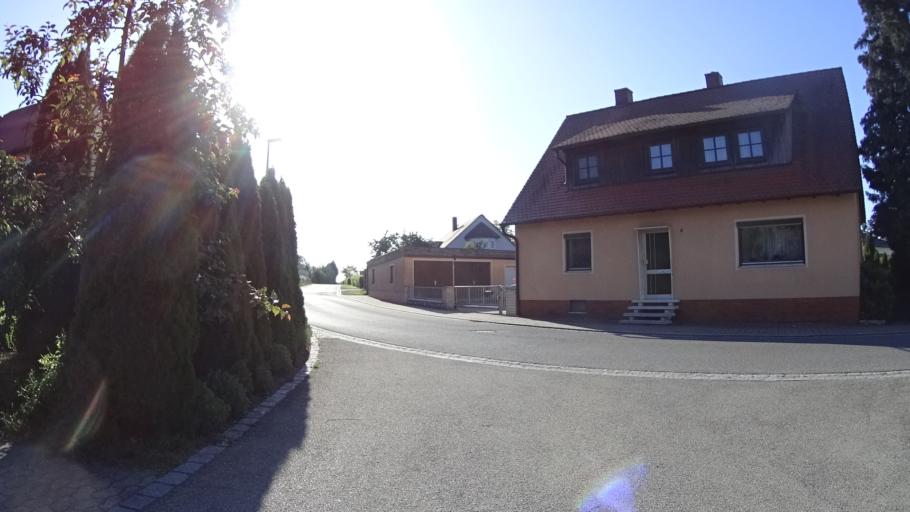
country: DE
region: Bavaria
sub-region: Regierungsbezirk Mittelfranken
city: Dentlein am Forst
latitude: 49.1479
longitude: 10.4246
